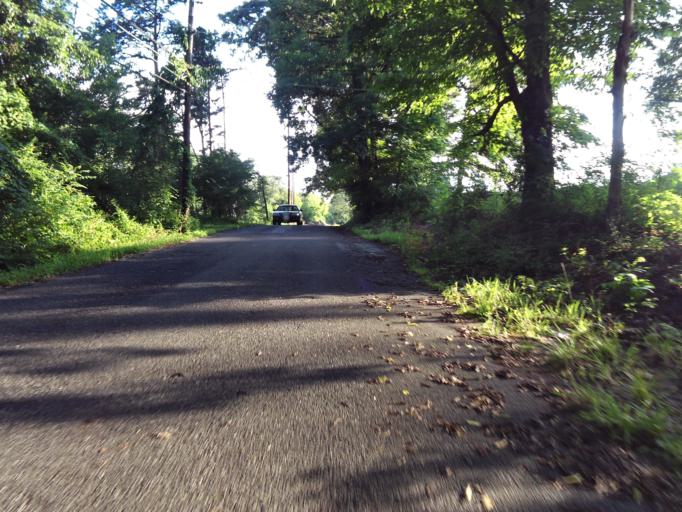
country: US
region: Tennessee
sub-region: Knox County
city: Knoxville
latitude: 36.0091
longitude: -83.9285
